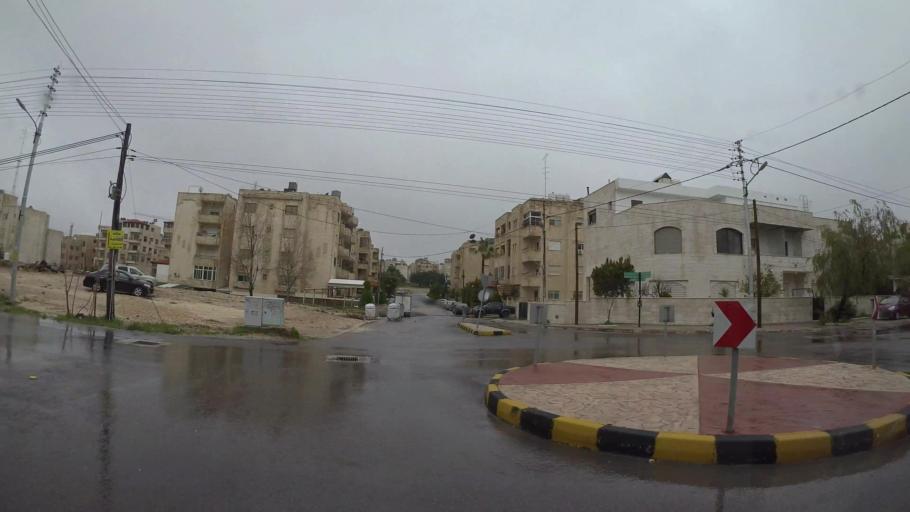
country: JO
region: Amman
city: Wadi as Sir
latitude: 31.9698
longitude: 35.8437
